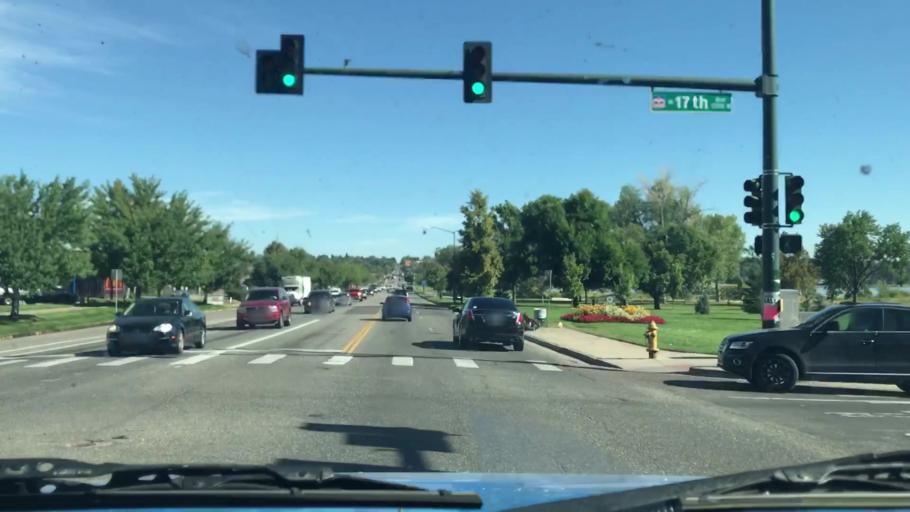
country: US
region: Colorado
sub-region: Jefferson County
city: Edgewater
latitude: 39.7439
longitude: -105.0532
